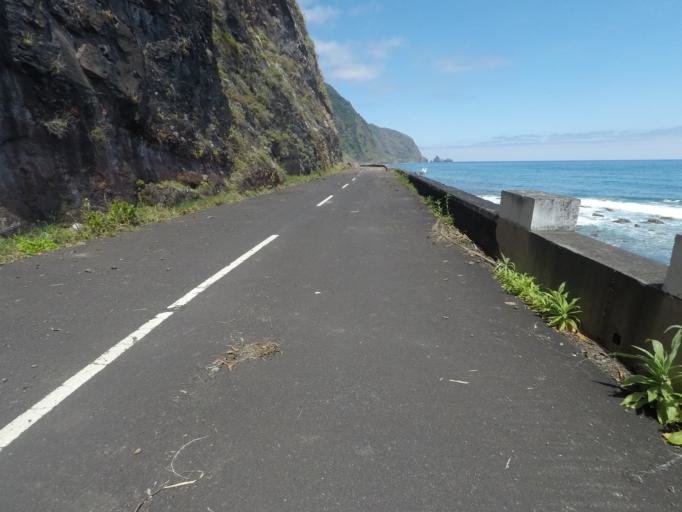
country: PT
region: Madeira
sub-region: Porto Moniz
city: Porto Moniz
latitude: 32.8267
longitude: -17.1234
